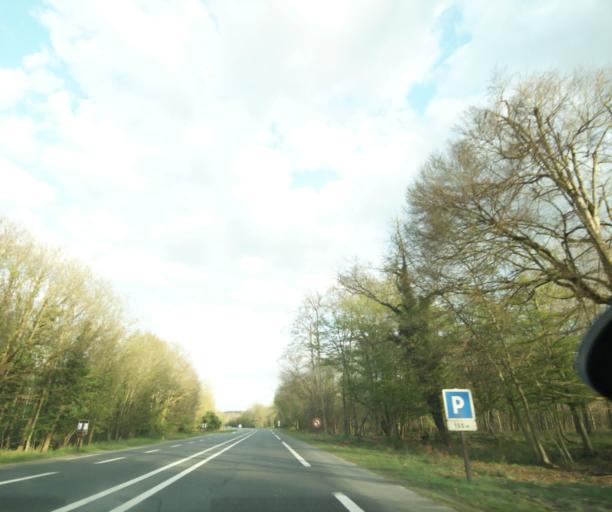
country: FR
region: Ile-de-France
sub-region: Departement de Seine-et-Marne
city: Barbizon
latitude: 48.4468
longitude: 2.6343
